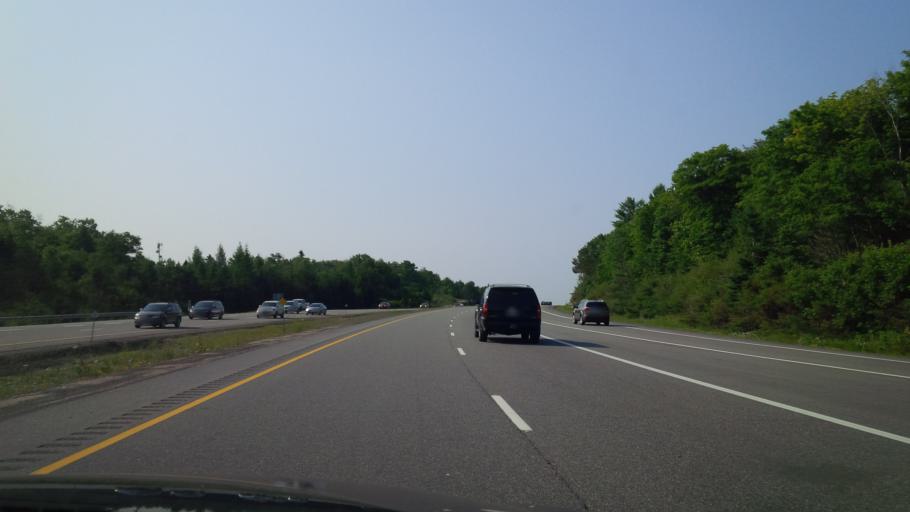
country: CA
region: Ontario
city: Bracebridge
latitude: 45.0830
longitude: -79.2969
